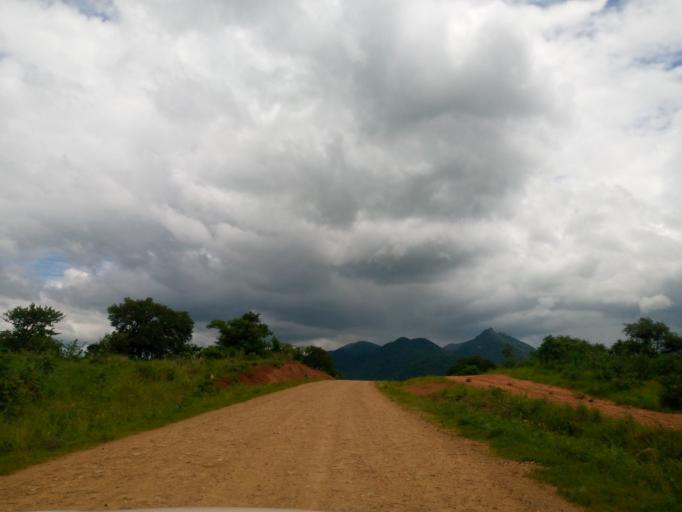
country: ET
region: Oromiya
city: Mendi
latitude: 10.1909
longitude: 35.0935
